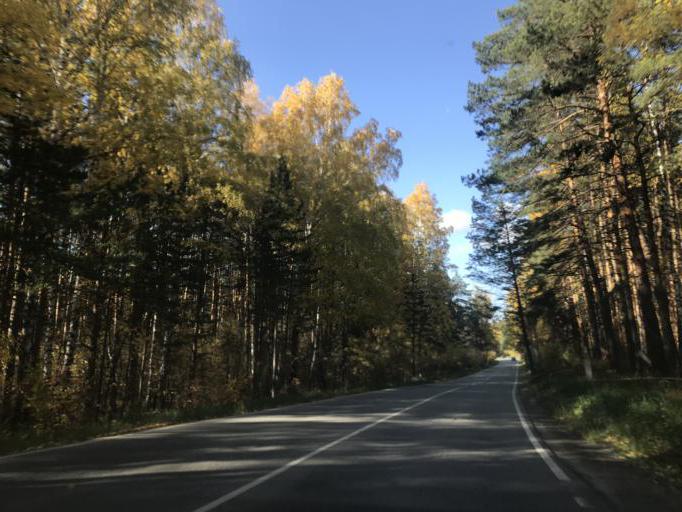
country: RU
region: Chelyabinsk
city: Dolgoderevenskoye
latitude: 55.2845
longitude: 61.3593
